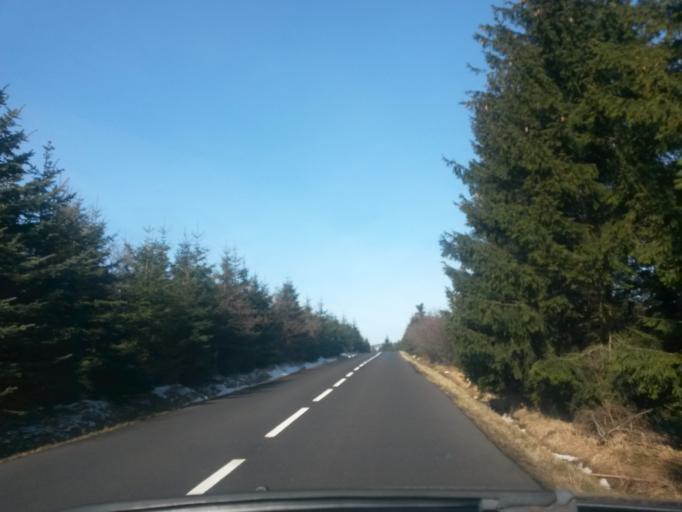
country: CZ
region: Ustecky
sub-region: Okres Chomutov
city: Kovarska
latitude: 50.4106
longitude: 13.0388
